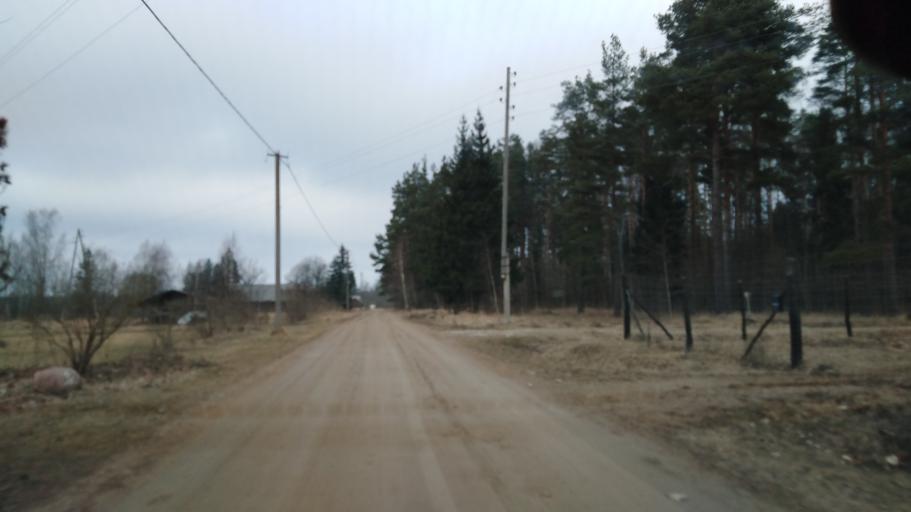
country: LV
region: Kuldigas Rajons
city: Kuldiga
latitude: 56.9863
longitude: 21.9705
